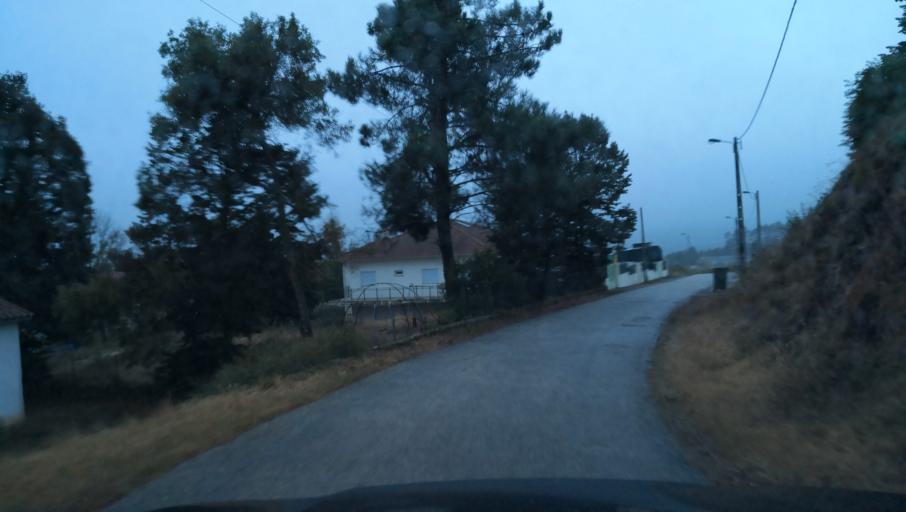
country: PT
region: Vila Real
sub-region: Sabrosa
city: Sabrosa
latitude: 41.2696
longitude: -7.6201
